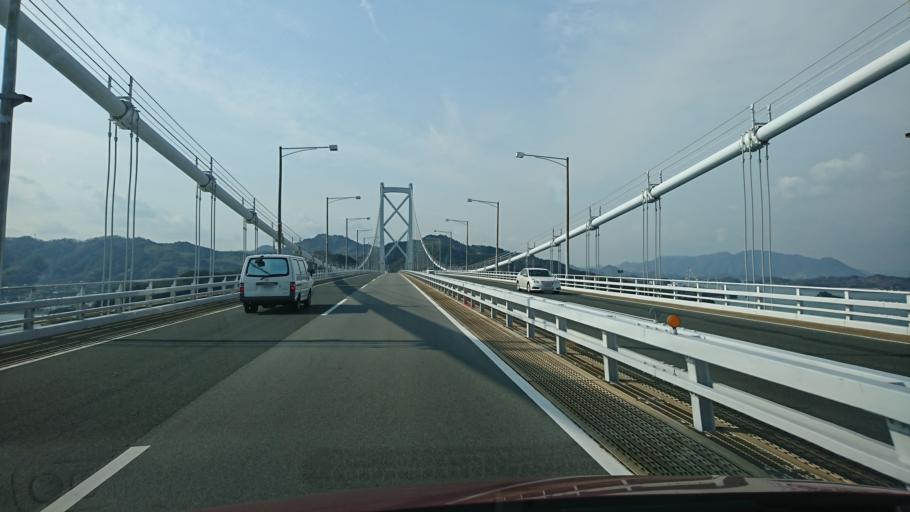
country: JP
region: Hiroshima
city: Onomichi
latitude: 34.3577
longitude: 133.1816
